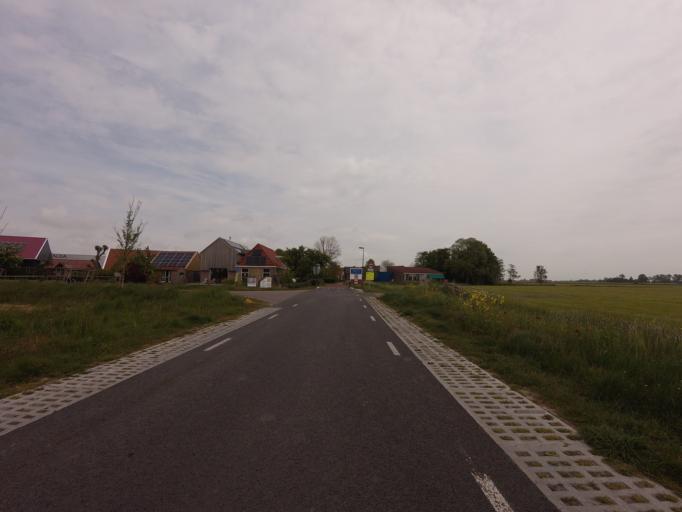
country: NL
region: Friesland
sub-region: Sudwest Fryslan
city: Bolsward
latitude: 53.0798
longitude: 5.4813
